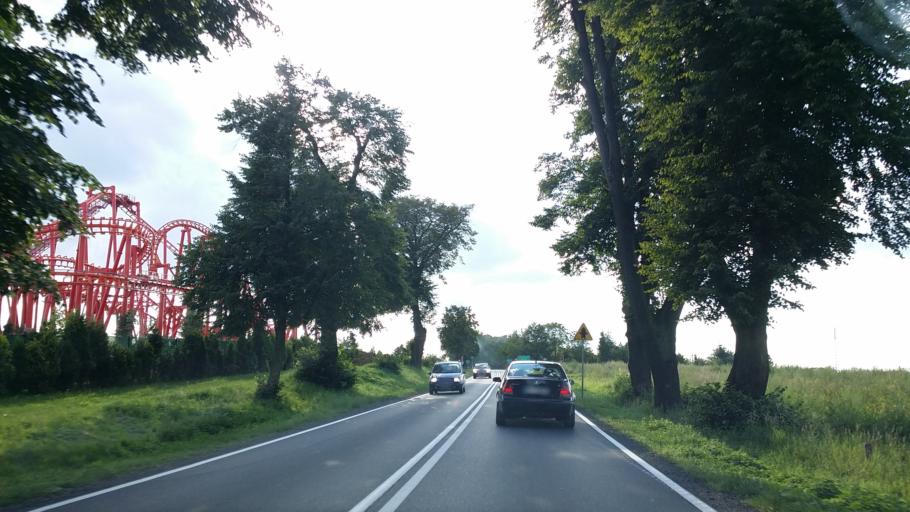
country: PL
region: Lesser Poland Voivodeship
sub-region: Powiat oswiecimski
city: Zator
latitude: 50.0020
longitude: 19.4074
